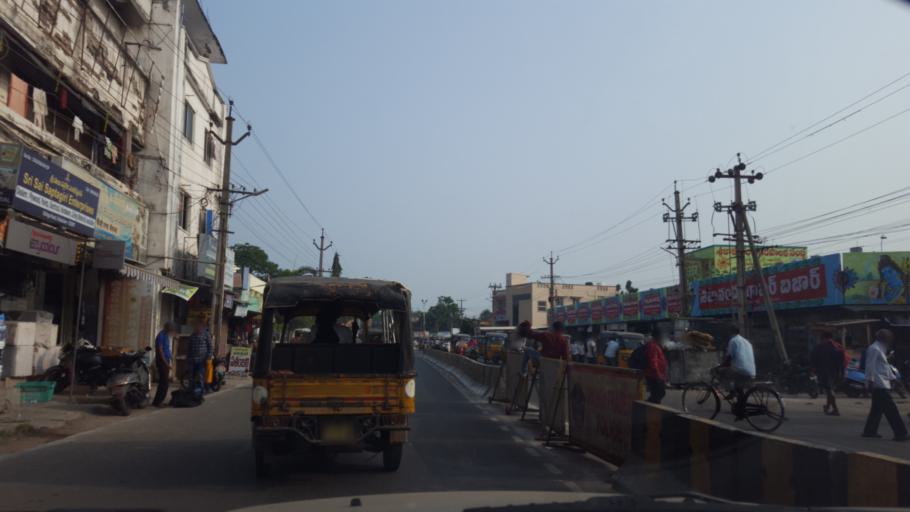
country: IN
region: Andhra Pradesh
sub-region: Srikakulam
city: Srikakulam
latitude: 18.2928
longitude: 83.8963
